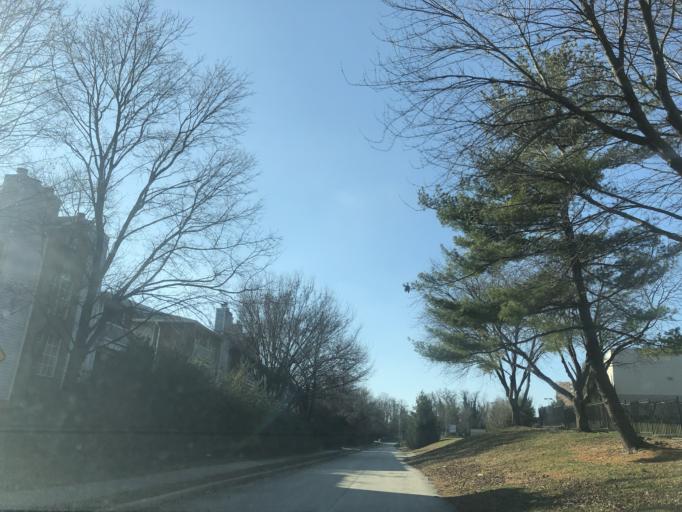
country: US
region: Pennsylvania
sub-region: Montgomery County
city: Bala-Cynwyd
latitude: 40.0064
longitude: -75.2100
